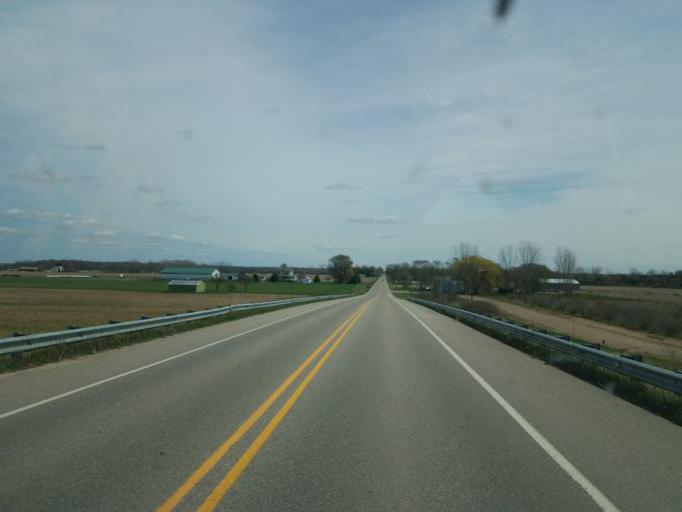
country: US
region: Michigan
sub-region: Isabella County
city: Mount Pleasant
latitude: 43.6406
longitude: -84.7580
